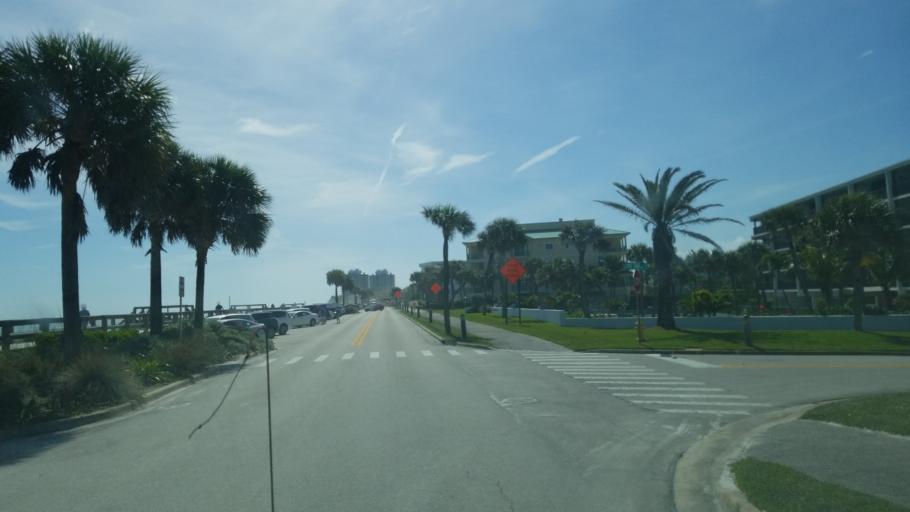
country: US
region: Florida
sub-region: Indian River County
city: Vero Beach
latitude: 27.6644
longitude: -80.3589
